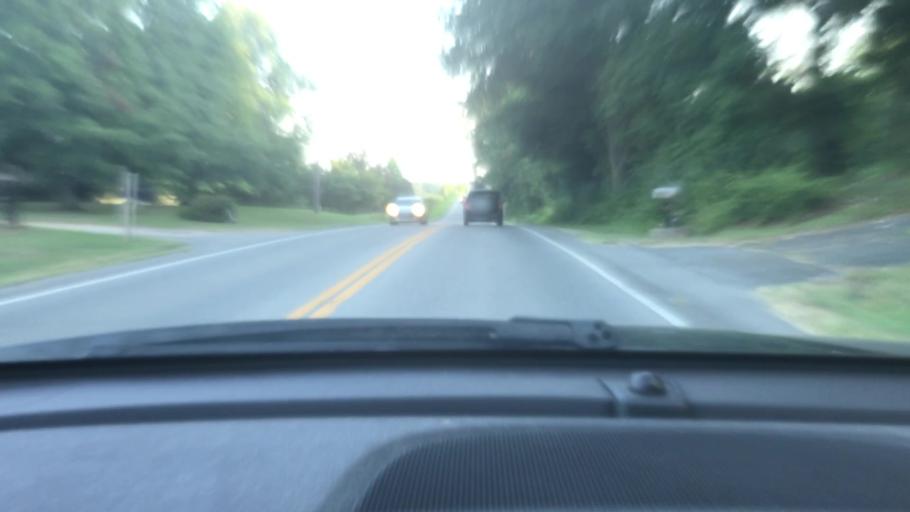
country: US
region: Tennessee
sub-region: Dickson County
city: Dickson
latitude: 36.0958
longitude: -87.3756
